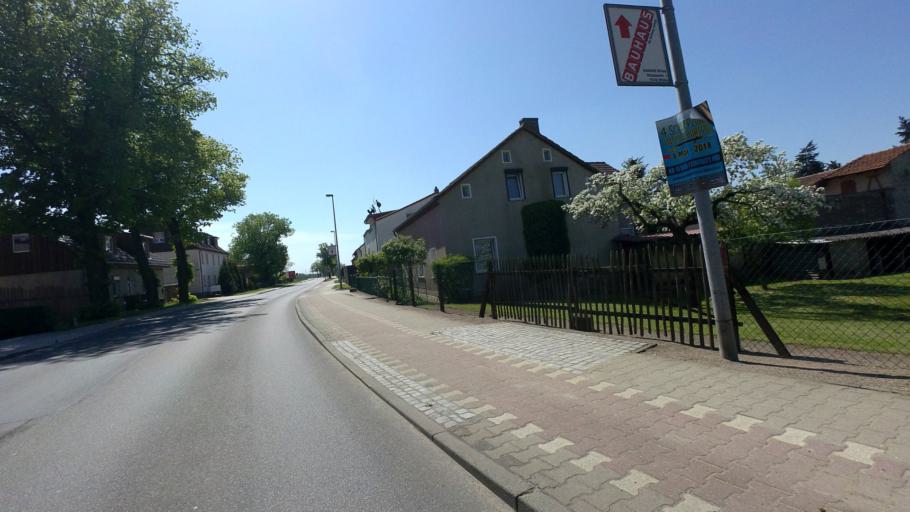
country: DE
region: Brandenburg
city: Schulzendorf
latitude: 52.3600
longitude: 13.5572
